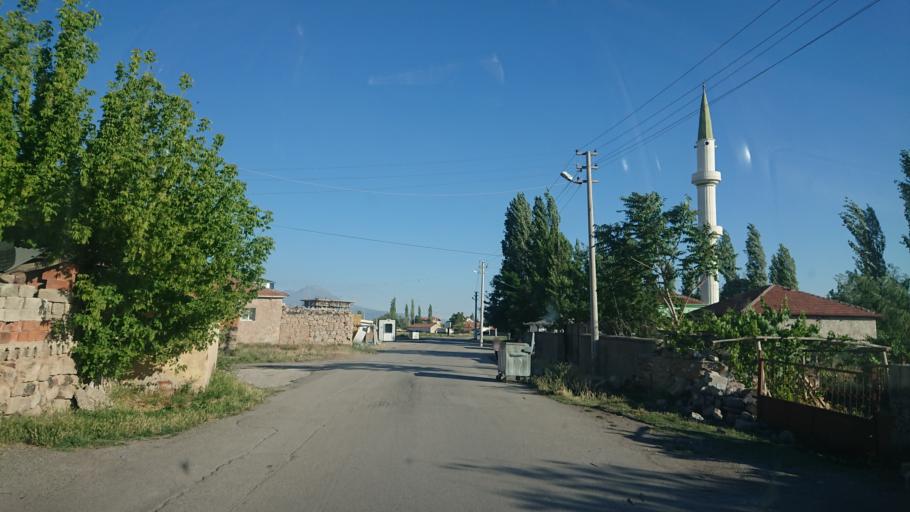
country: TR
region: Aksaray
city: Aksaray
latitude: 38.3842
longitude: 33.9908
